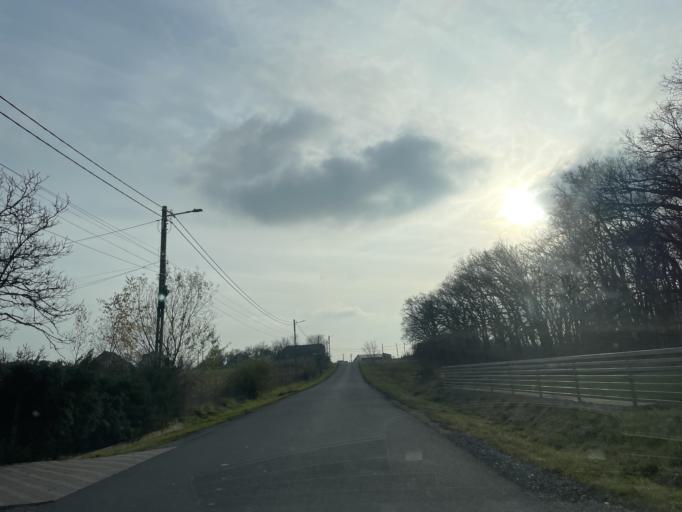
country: RO
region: Mures
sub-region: Comuna Solovastru
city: Solovastru
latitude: 46.7725
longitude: 24.7608
